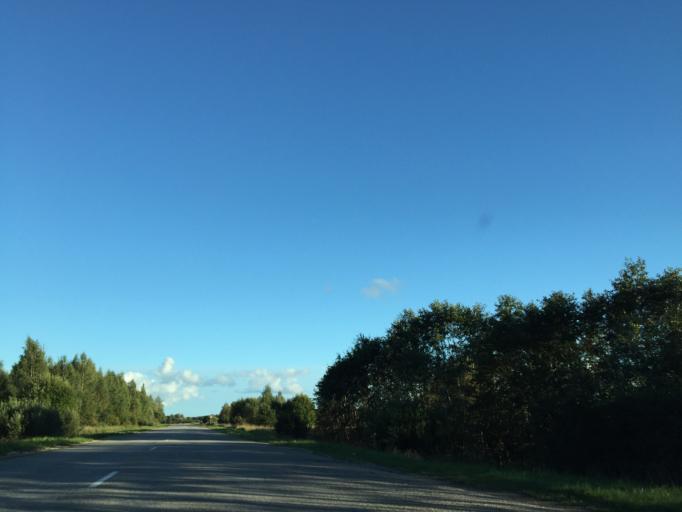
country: LV
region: Kuldigas Rajons
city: Kuldiga
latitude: 56.9410
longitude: 22.0242
